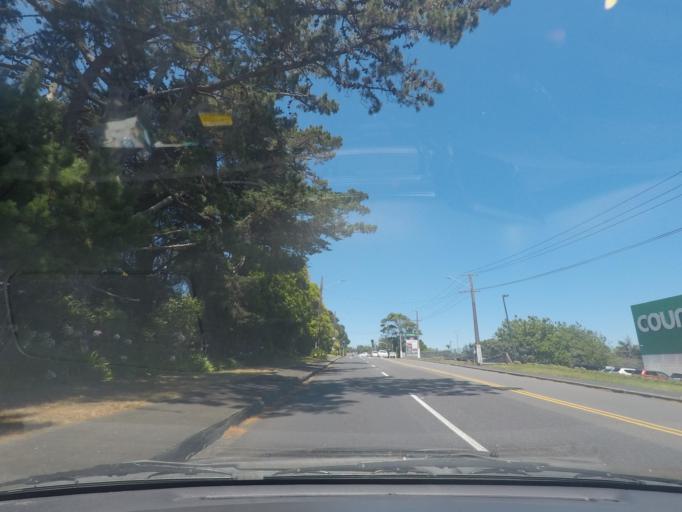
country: NZ
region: Auckland
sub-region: Auckland
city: Waitakere
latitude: -36.9248
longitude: 174.7234
